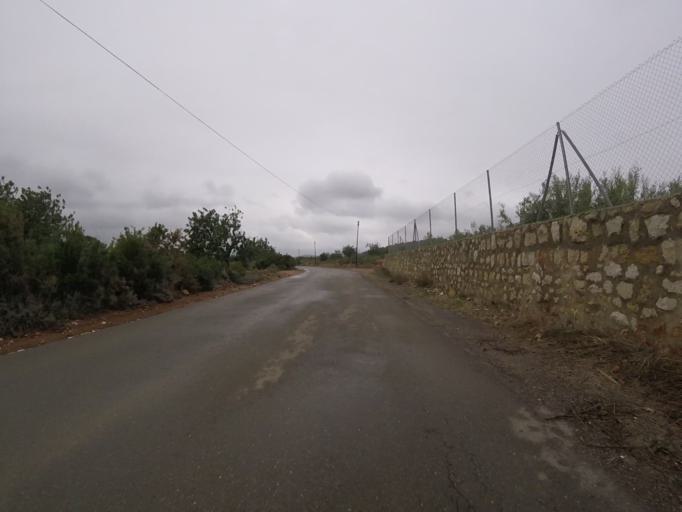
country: ES
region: Valencia
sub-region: Provincia de Castello
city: Alcoceber
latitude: 40.2419
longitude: 0.2491
